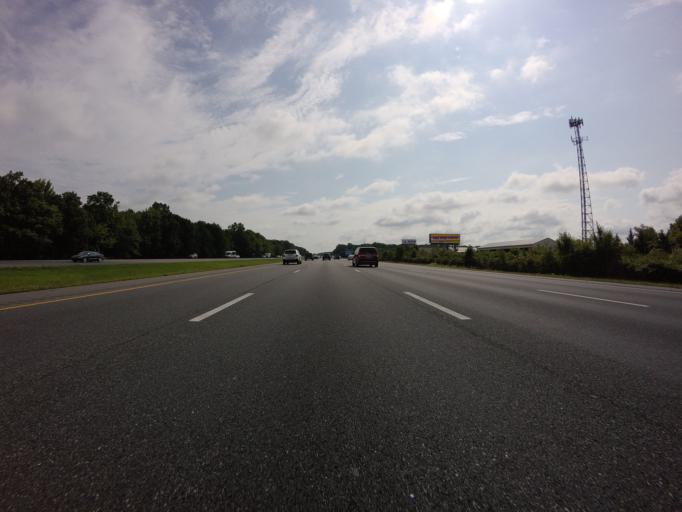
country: US
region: Delaware
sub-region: New Castle County
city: Brookside
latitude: 39.6518
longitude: -75.7168
